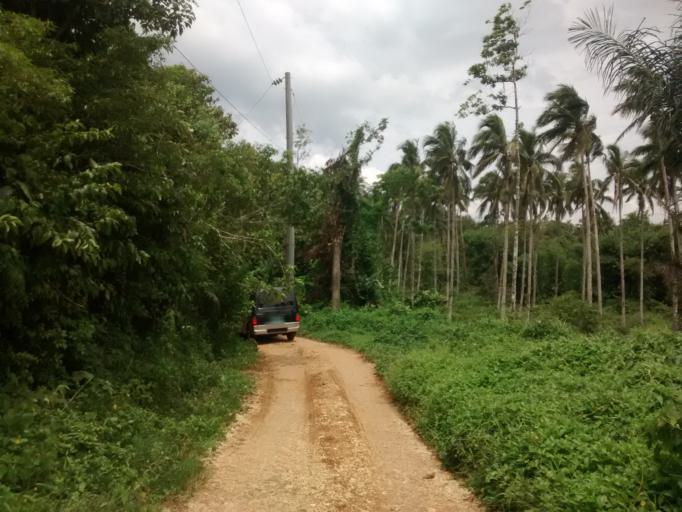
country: PH
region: Calabarzon
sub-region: Province of Quezon
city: Lucban
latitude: 14.1543
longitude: 121.5575
